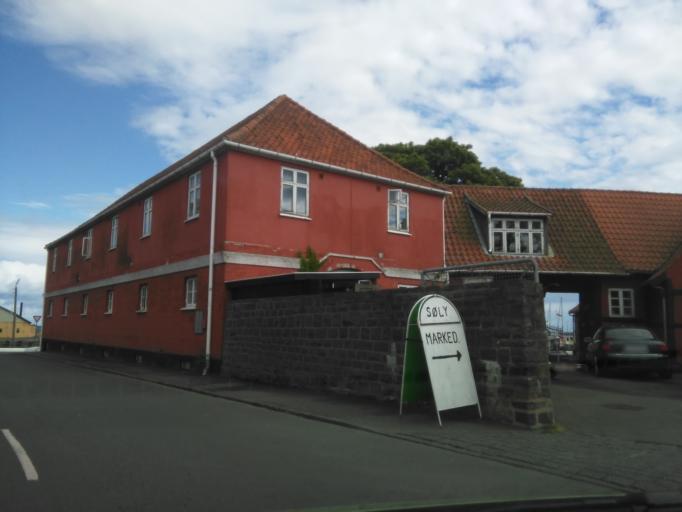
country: DK
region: Capital Region
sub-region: Bornholm Kommune
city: Nexo
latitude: 55.0638
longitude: 15.1339
